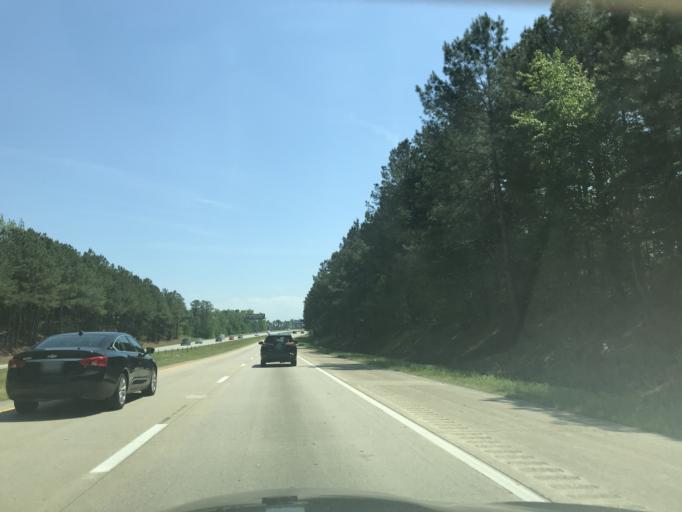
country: US
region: North Carolina
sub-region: Johnston County
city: Benson
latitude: 35.4142
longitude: -78.5259
